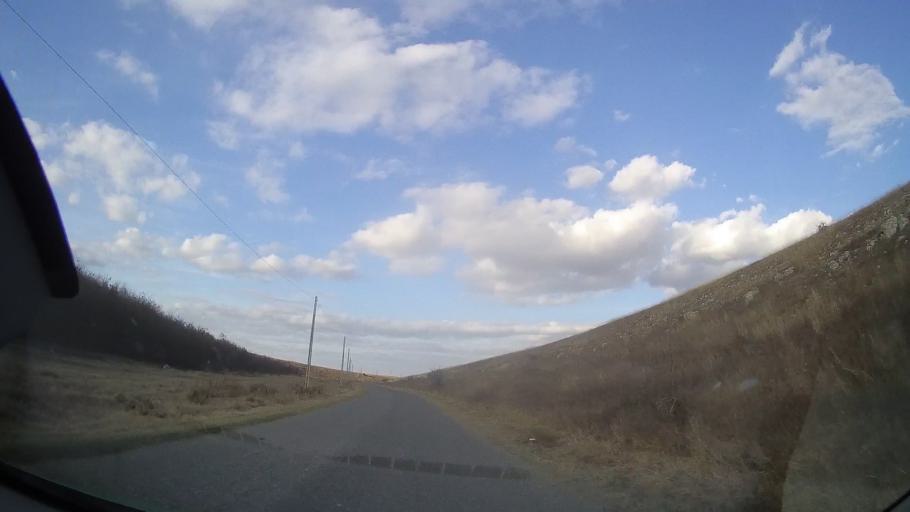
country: RO
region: Constanta
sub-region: Comuna Cerchezu
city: Cerchezu
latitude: 43.8355
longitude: 28.0975
